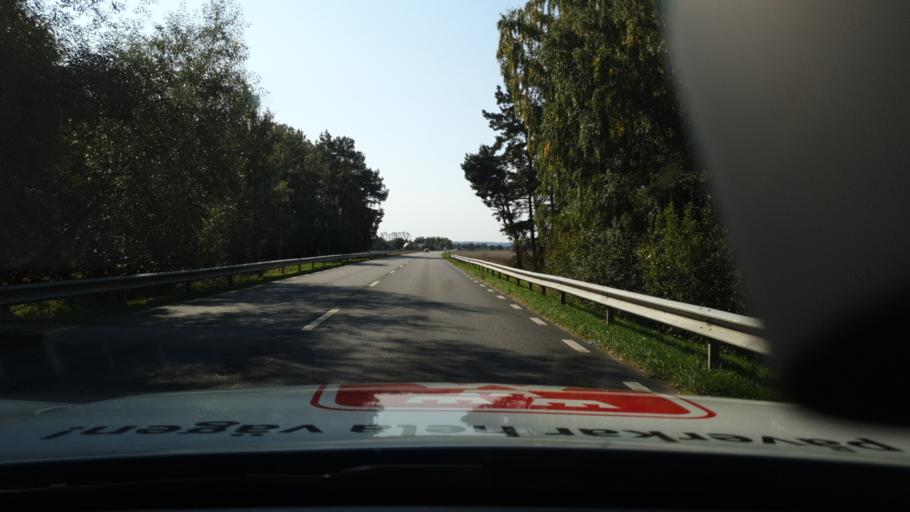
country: SE
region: Skane
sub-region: Kristianstads Kommun
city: Ahus
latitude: 55.8752
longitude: 14.2200
